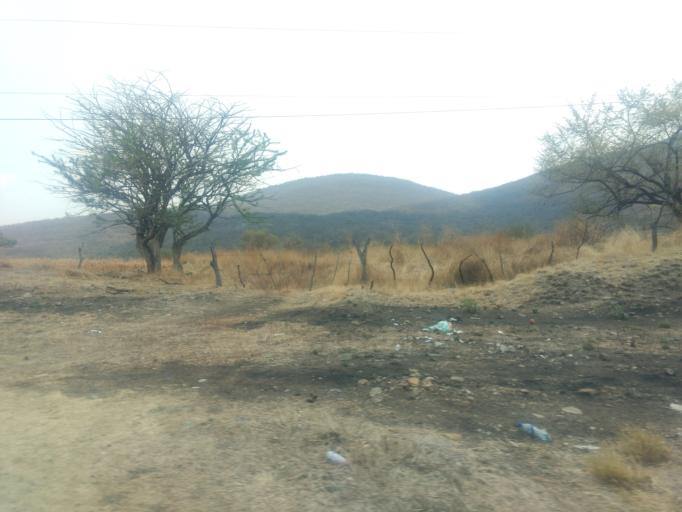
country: MX
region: Morelos
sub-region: Mazatepec
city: Cuauchichinola
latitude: 18.6569
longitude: -99.4117
